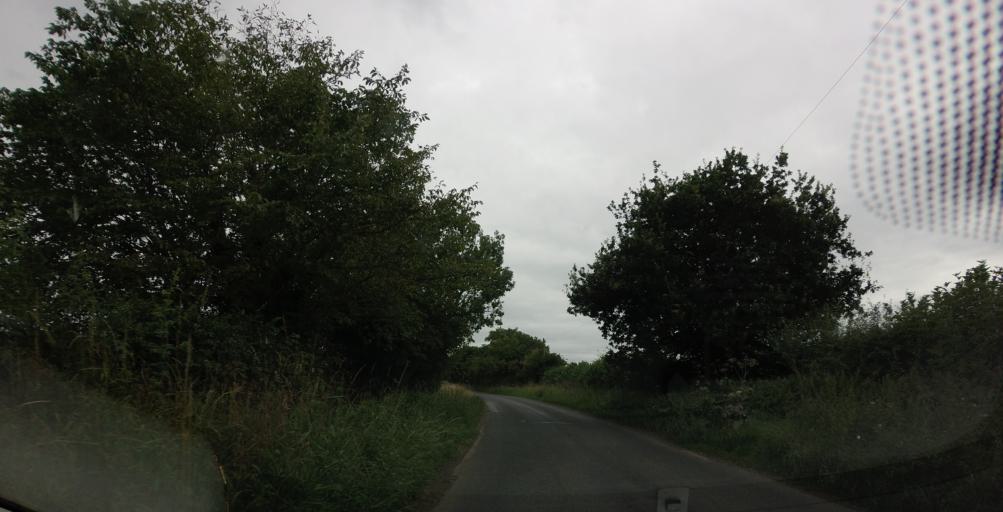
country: GB
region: England
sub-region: North Yorkshire
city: Ripon
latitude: 54.1043
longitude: -1.5169
